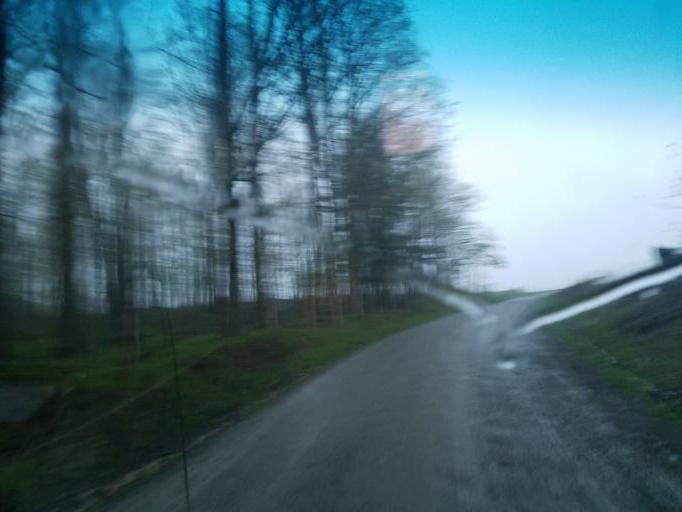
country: US
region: Pennsylvania
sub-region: Tioga County
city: Westfield
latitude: 41.9346
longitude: -77.6936
